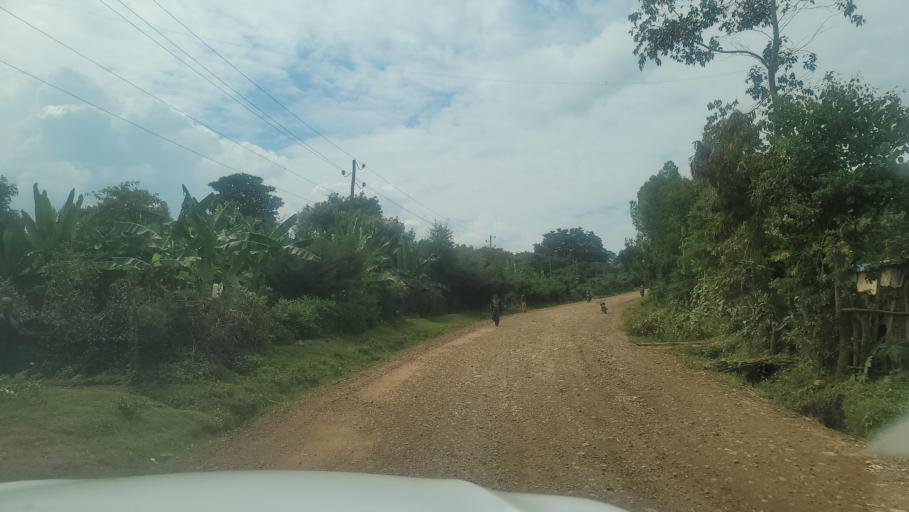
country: ET
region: Oromiya
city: Agaro
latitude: 7.8298
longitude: 36.5431
